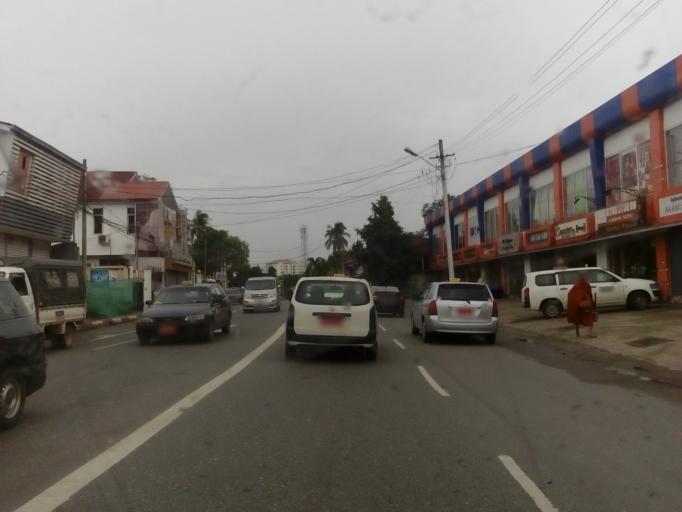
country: MM
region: Yangon
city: Yangon
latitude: 16.8516
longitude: 96.1509
